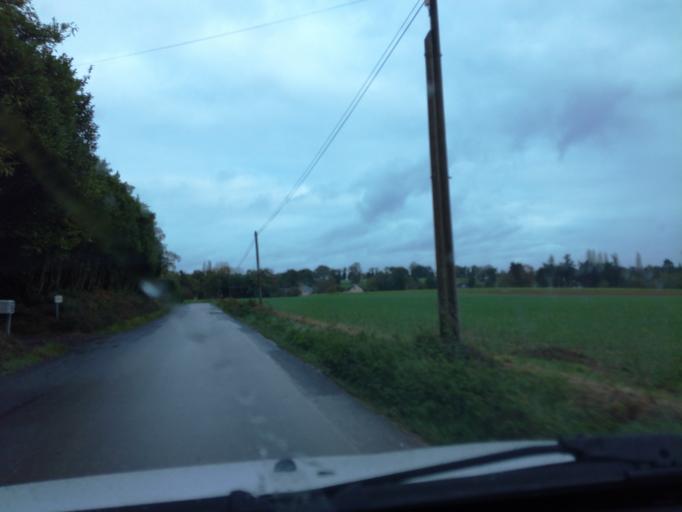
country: FR
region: Brittany
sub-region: Departement d'Ille-et-Vilaine
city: Montgermont
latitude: 48.1755
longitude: -1.7070
